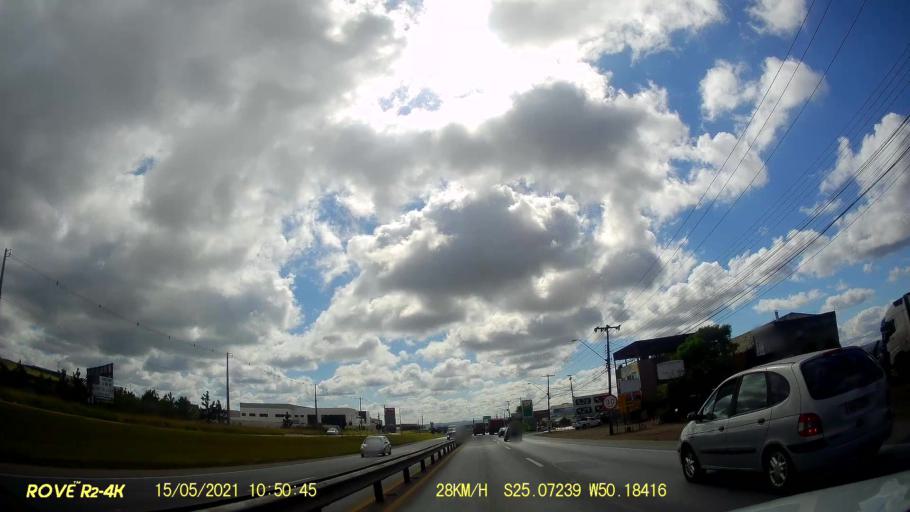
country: BR
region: Parana
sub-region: Ponta Grossa
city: Ponta Grossa
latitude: -25.0723
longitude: -50.1842
